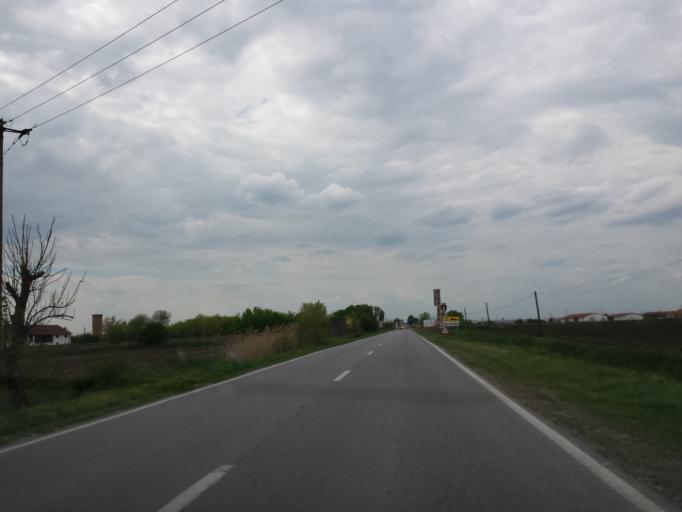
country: RO
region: Timis
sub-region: Comuna Sanpetru Mare
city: Sanpetru Mare
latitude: 46.0483
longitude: 20.6487
